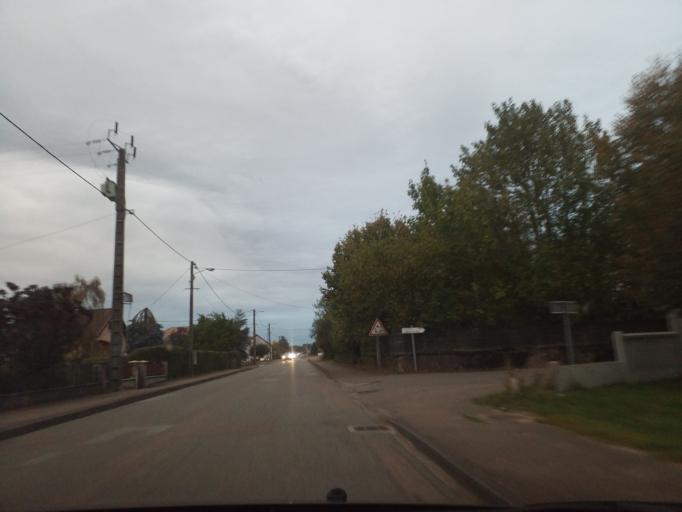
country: FR
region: Franche-Comte
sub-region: Departement de la Haute-Saone
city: Saint-Germain
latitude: 47.7255
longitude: 6.5359
